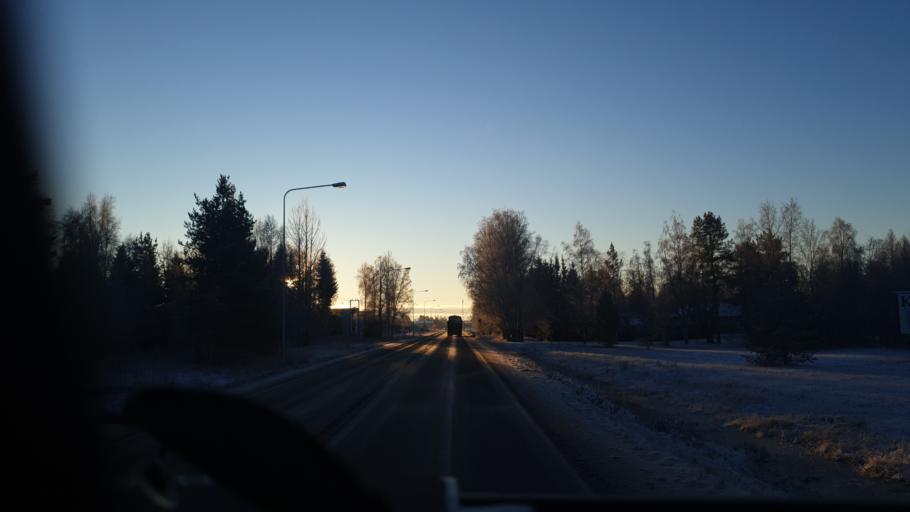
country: FI
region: Northern Ostrobothnia
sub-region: Ylivieska
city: Kalajoki
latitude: 64.2698
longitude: 23.9491
